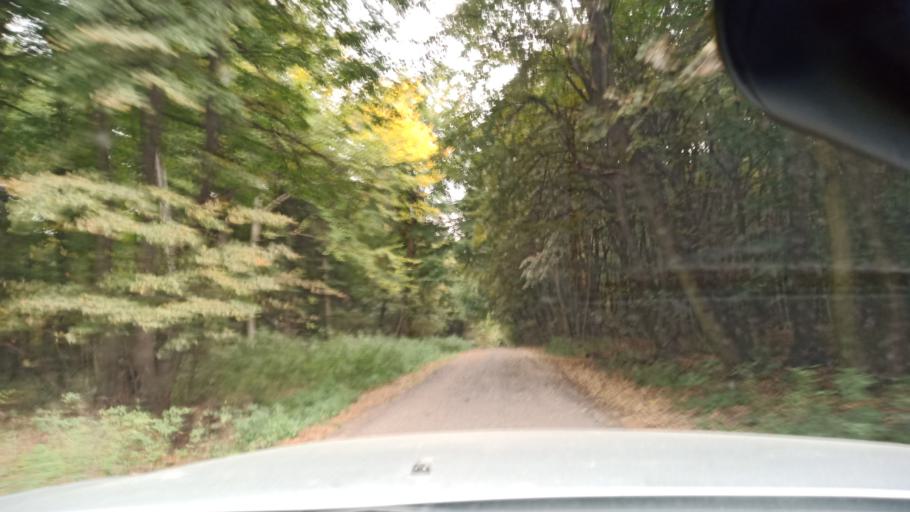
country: HU
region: Fejer
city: Pusztavam
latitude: 47.3838
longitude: 18.2784
